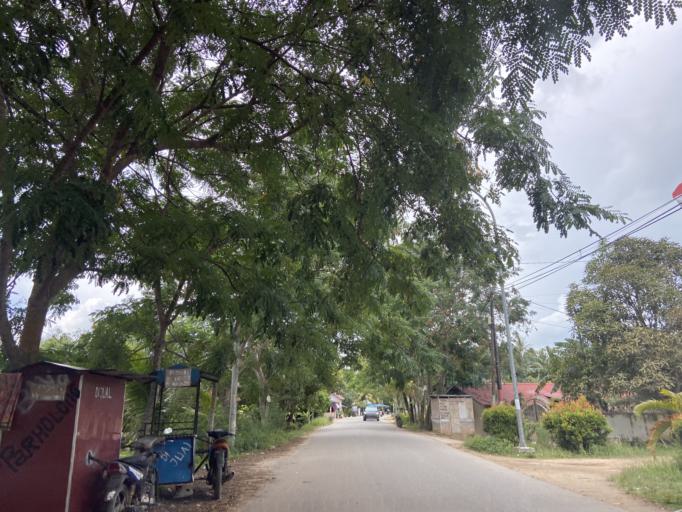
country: SG
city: Singapore
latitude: 1.1520
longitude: 104.1346
